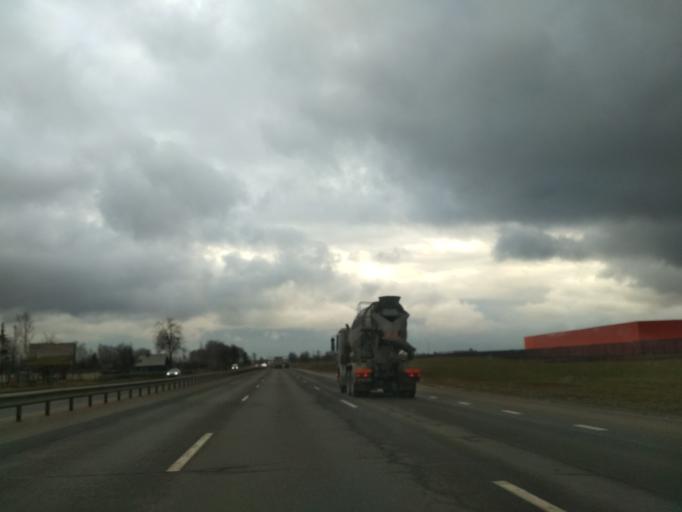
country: BY
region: Minsk
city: Pryvol'ny
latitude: 53.8107
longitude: 27.7813
